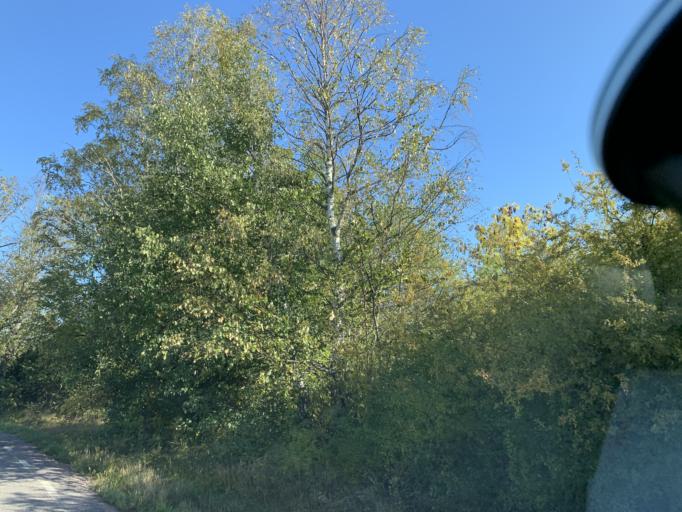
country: SE
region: Vaestmanland
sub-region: Vasteras
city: Vasteras
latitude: 59.5709
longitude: 16.4542
